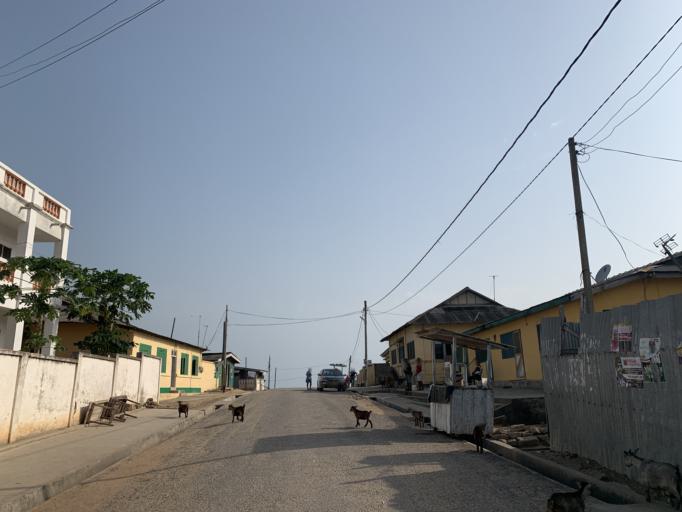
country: GH
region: Central
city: Winneba
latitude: 5.3364
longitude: -0.6223
